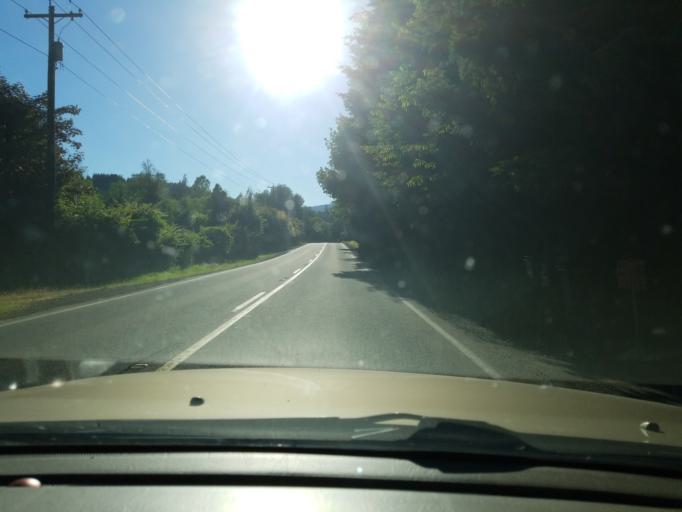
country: US
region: Oregon
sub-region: Yamhill County
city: McMinnville
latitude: 45.2263
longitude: -123.2674
